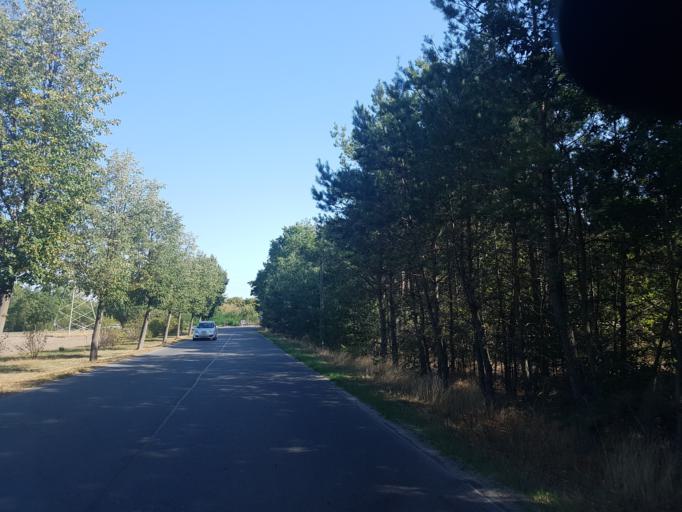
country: DE
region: Brandenburg
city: Finsterwalde
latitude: 51.6384
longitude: 13.7398
